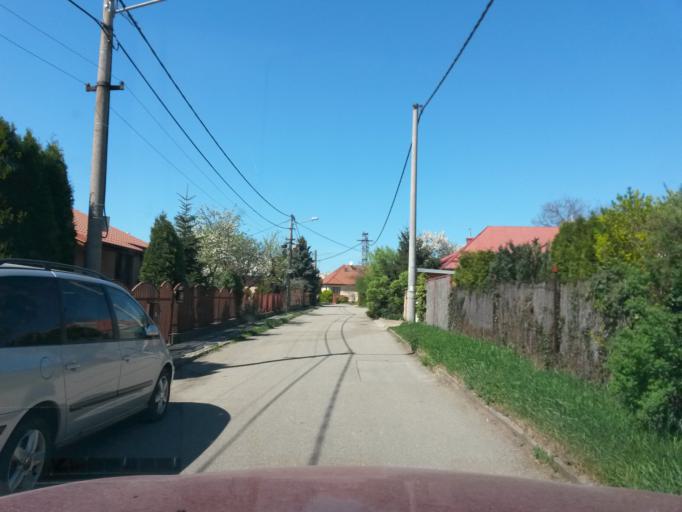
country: SK
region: Kosicky
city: Kosice
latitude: 48.6784
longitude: 21.2734
